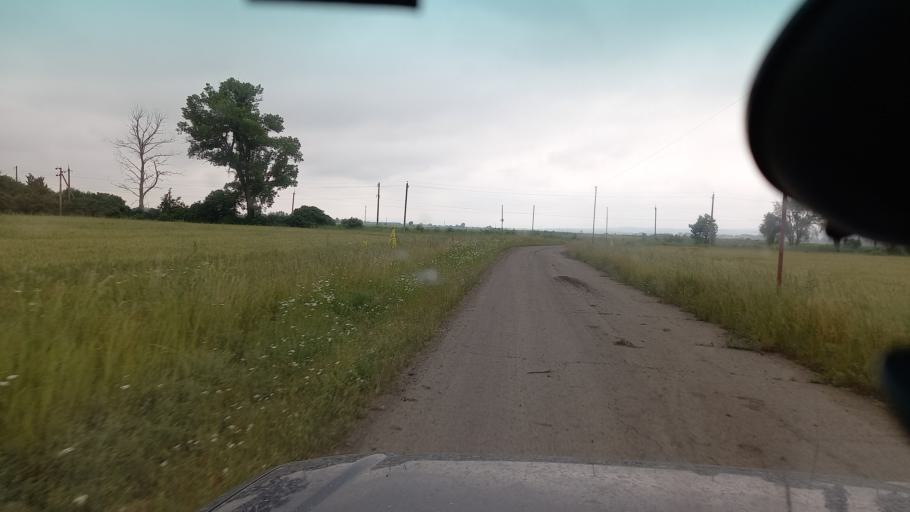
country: RU
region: Krasnodarskiy
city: Mostovskoy
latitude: 44.4242
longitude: 40.7539
